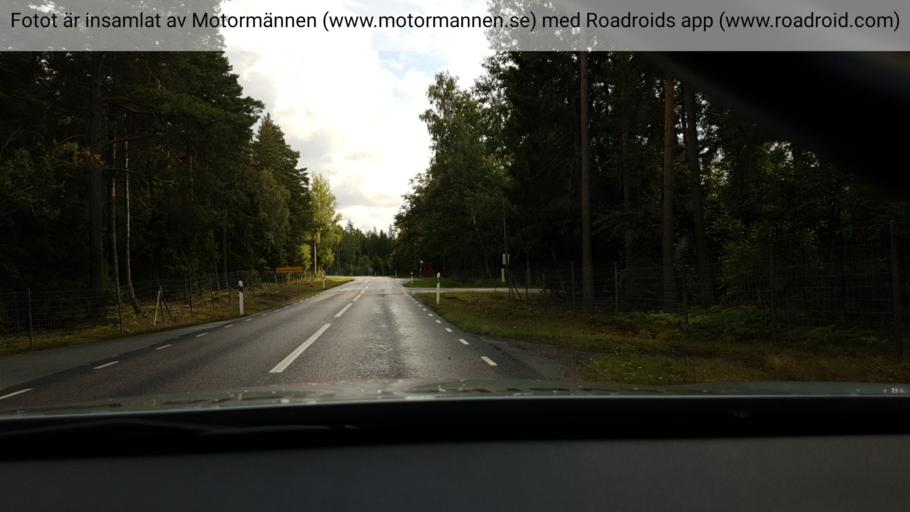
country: SE
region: Stockholm
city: Stenhamra
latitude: 59.3079
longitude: 17.6417
